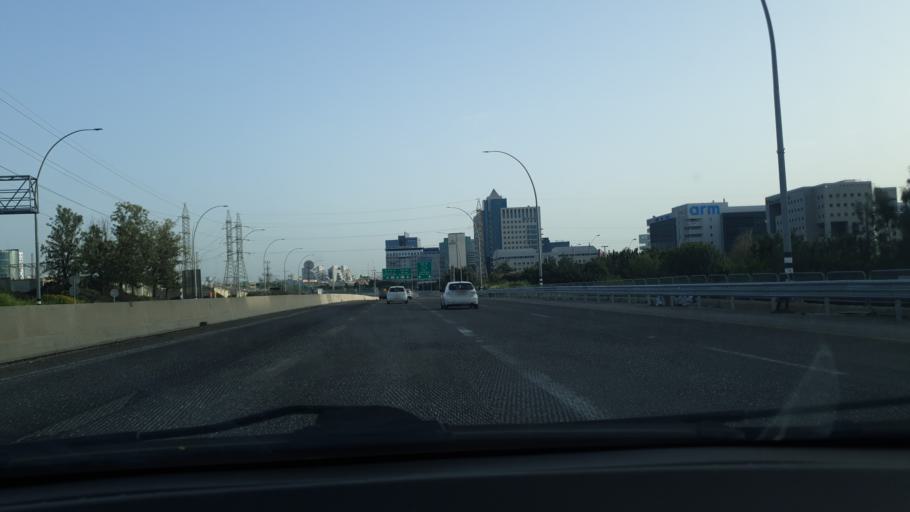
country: IL
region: Central District
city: Ra'anana
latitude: 32.2012
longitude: 34.8845
